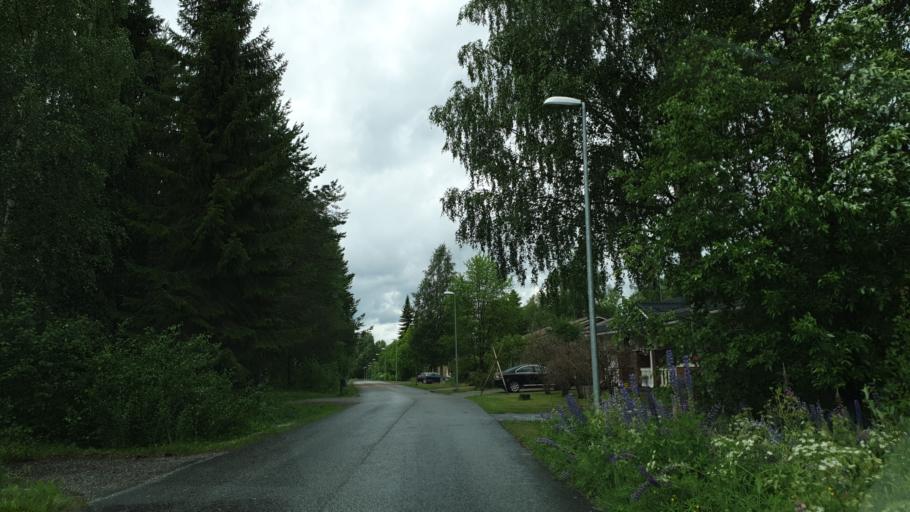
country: FI
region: Kainuu
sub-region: Kehys-Kainuu
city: Kuhmo
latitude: 64.1187
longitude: 29.5117
